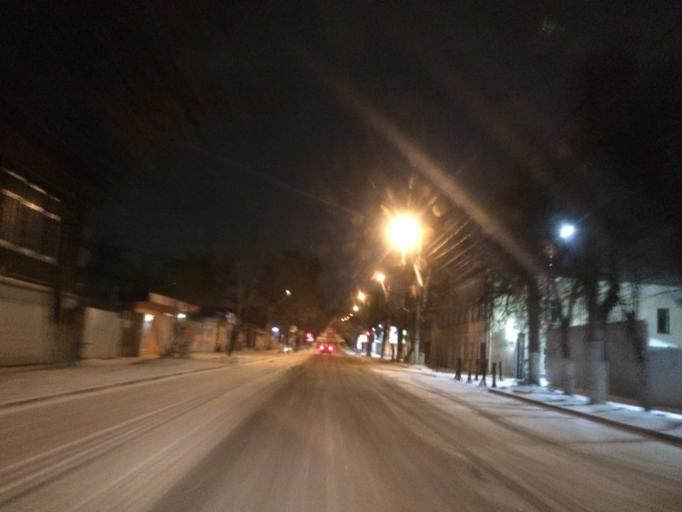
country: RU
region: Tula
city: Tula
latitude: 54.1887
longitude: 37.6161
